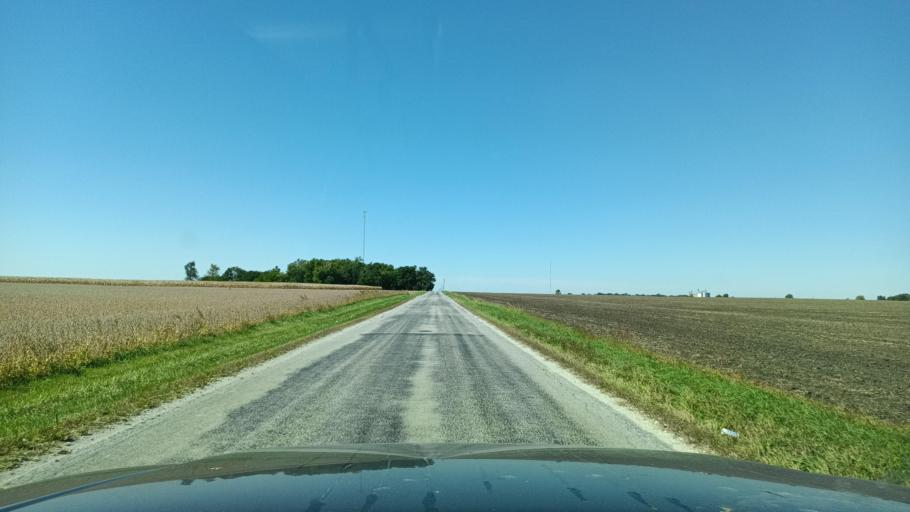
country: US
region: Illinois
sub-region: Champaign County
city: Mahomet
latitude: 40.0987
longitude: -88.3934
